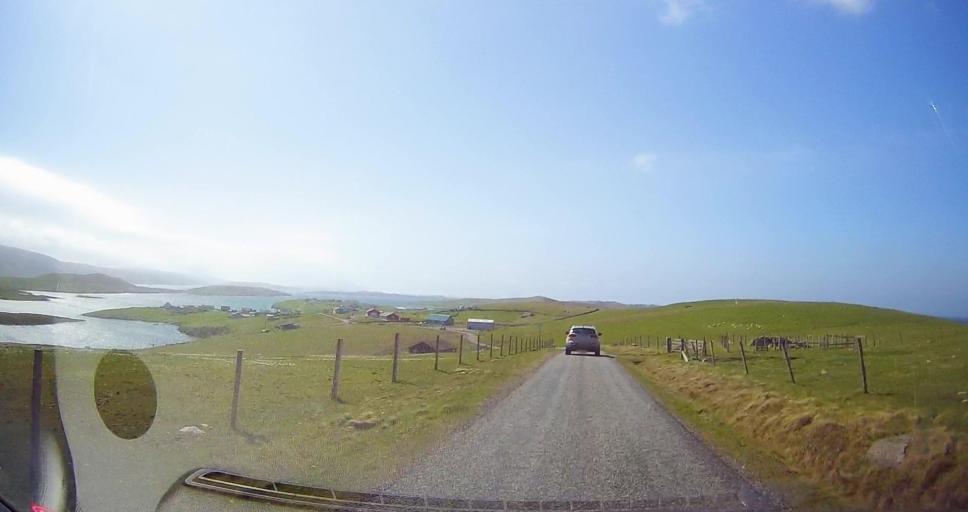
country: GB
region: Scotland
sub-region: Shetland Islands
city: Sandwick
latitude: 60.0740
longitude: -1.3386
